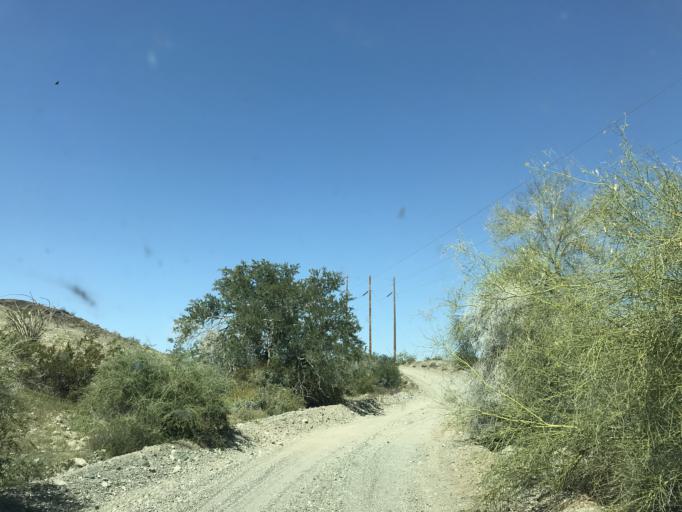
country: US
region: California
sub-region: Riverside County
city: Mesa Verde
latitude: 33.4972
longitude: -114.8408
